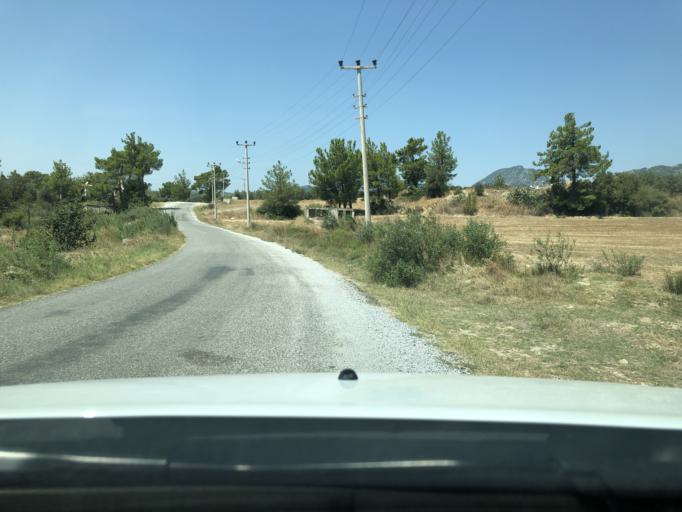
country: TR
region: Antalya
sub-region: Manavgat
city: Kizilagac
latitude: 36.8557
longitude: 31.5660
